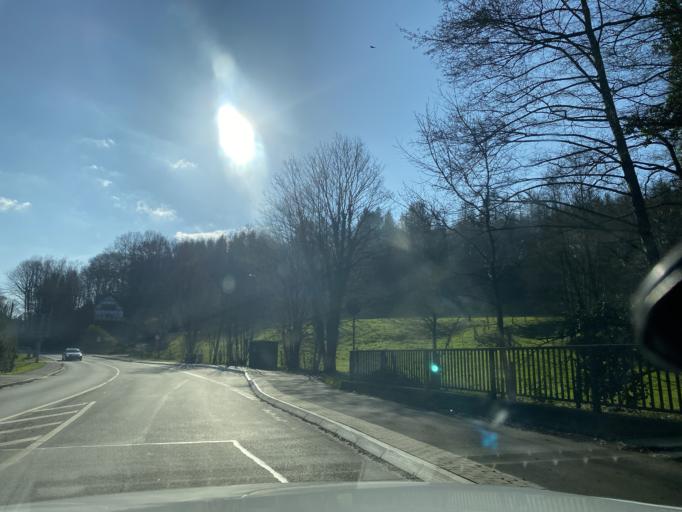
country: DE
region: North Rhine-Westphalia
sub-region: Regierungsbezirk Koln
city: Odenthal
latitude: 51.0265
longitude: 7.1185
